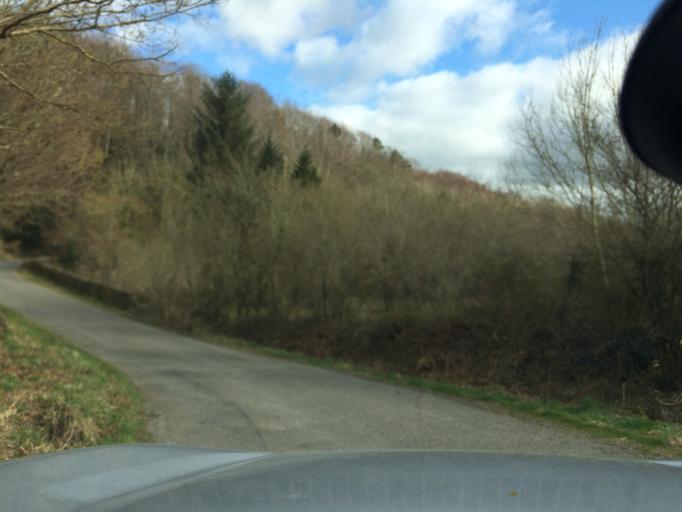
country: IE
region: Munster
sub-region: Waterford
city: Portlaw
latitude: 52.2799
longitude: -7.3717
